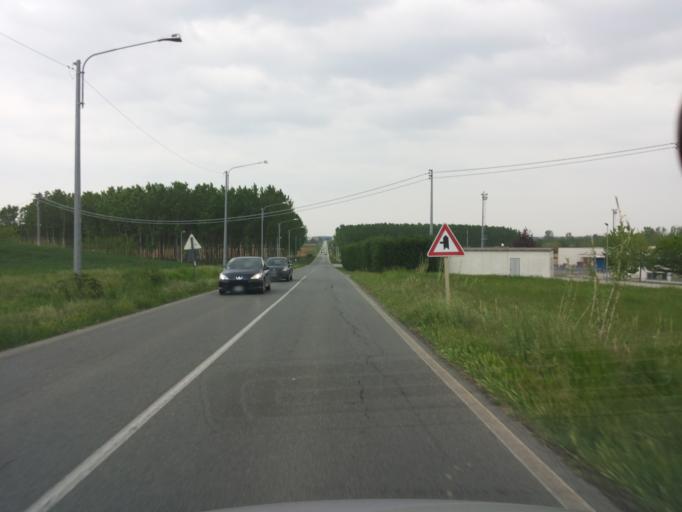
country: IT
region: Piedmont
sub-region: Provincia di Alessandria
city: Mirabello Monferrato
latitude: 45.0409
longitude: 8.5236
